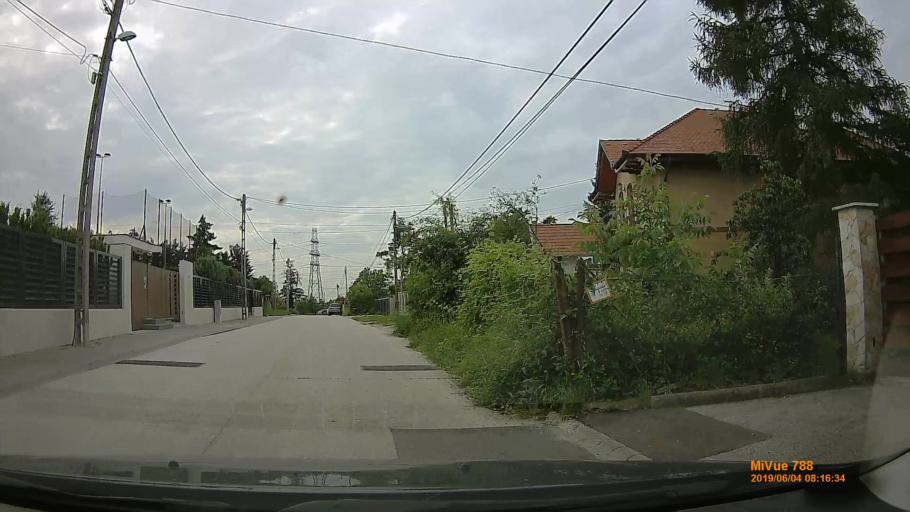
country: HU
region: Budapest
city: Budapest XXII. keruelet
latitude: 47.4356
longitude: 19.0232
